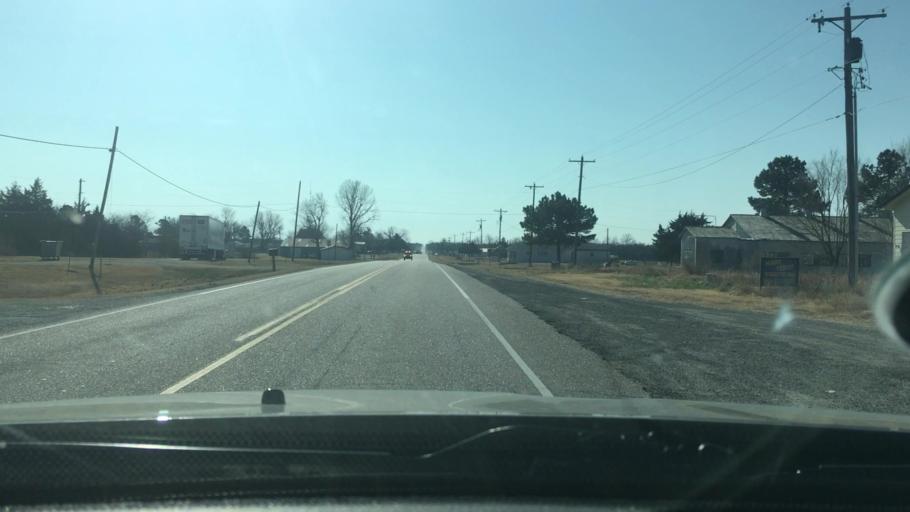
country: US
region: Oklahoma
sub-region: Garvin County
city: Stratford
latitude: 34.8027
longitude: -96.9676
